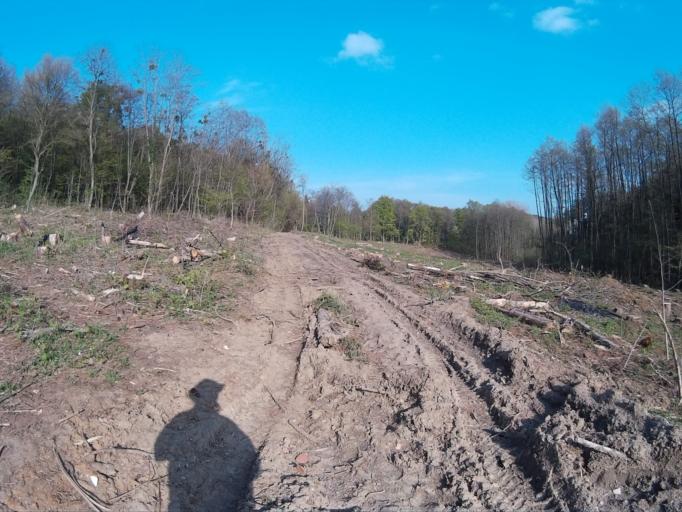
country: AT
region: Burgenland
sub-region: Politischer Bezirk Oberwart
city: Rechnitz
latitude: 47.3387
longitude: 16.4815
